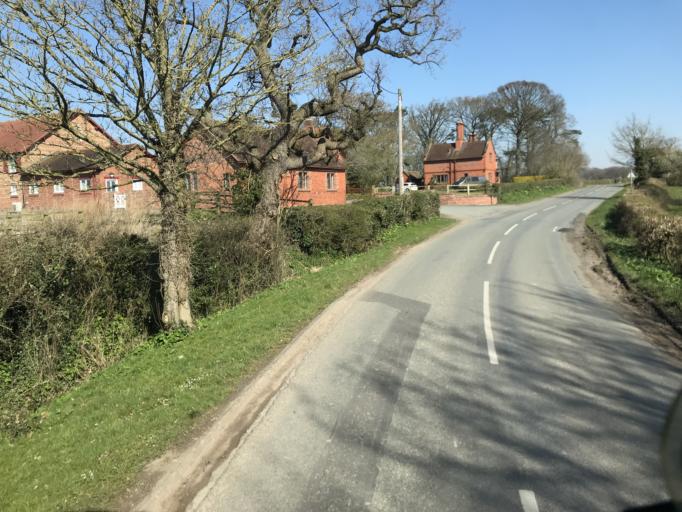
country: GB
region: England
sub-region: Cheshire West and Chester
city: Aldford
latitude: 53.1441
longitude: -2.8425
